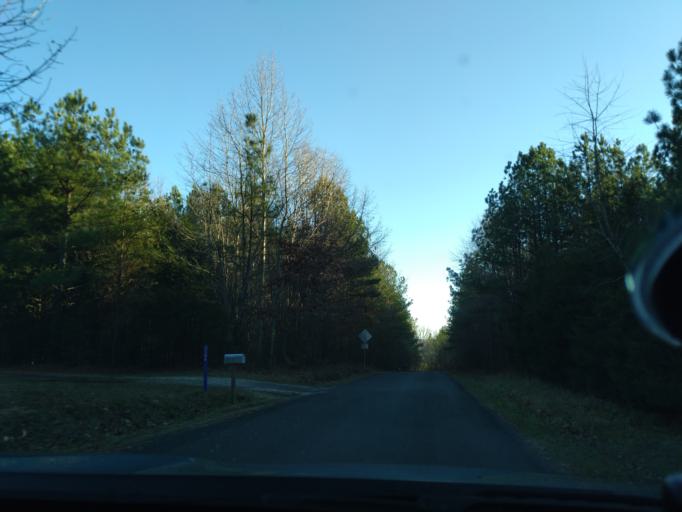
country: US
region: Virginia
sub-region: Buckingham County
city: Buckingham
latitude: 37.3651
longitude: -78.6108
